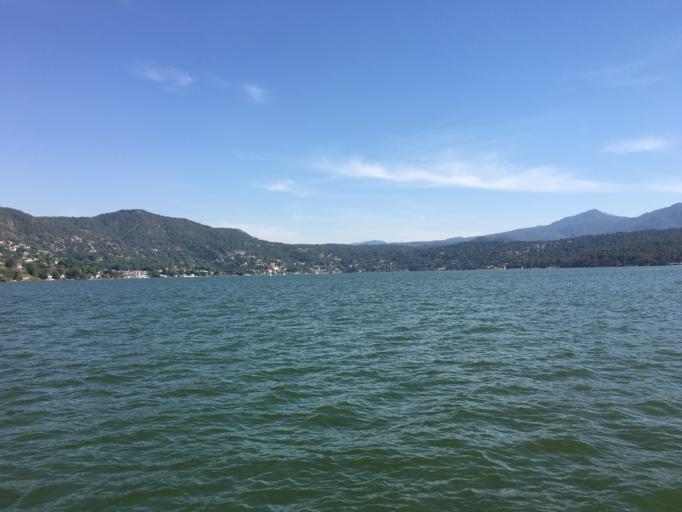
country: MX
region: Mexico
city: Valle de Bravo
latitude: 19.1934
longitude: -100.1508
